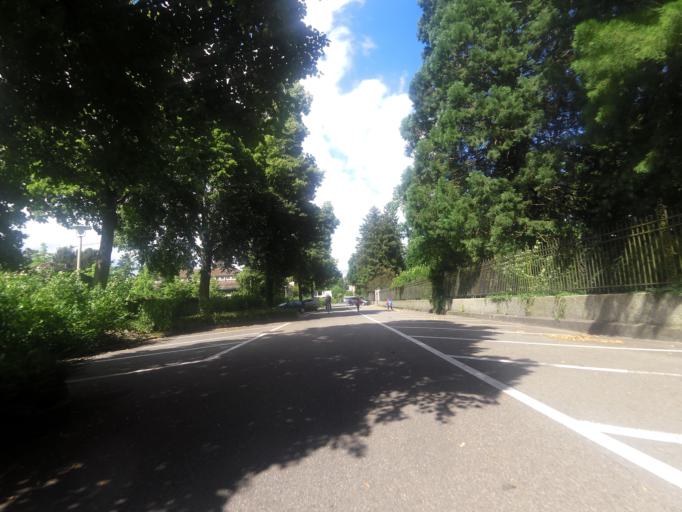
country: CH
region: Zurich
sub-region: Bezirk Zuerich
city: Zuerich (Kreis 3) / Sihlfeld
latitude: 47.3763
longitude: 8.5063
